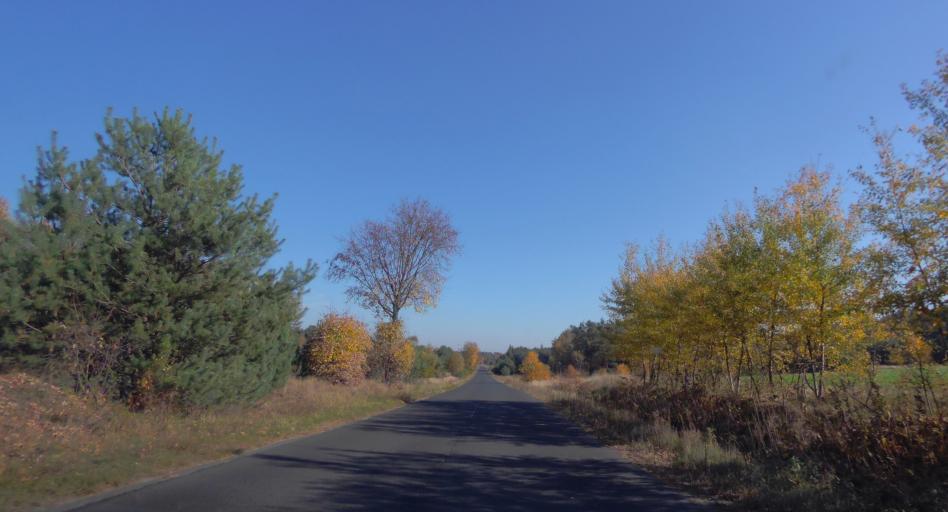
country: PL
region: Subcarpathian Voivodeship
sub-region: Powiat lezajski
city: Wola Zarczycka
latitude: 50.3019
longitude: 22.2910
